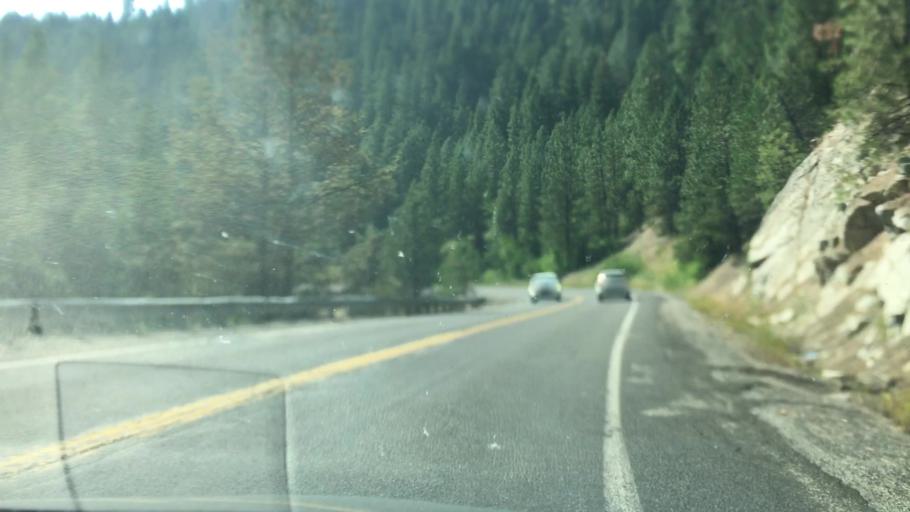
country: US
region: Idaho
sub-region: Valley County
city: Cascade
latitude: 44.2507
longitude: -116.0897
